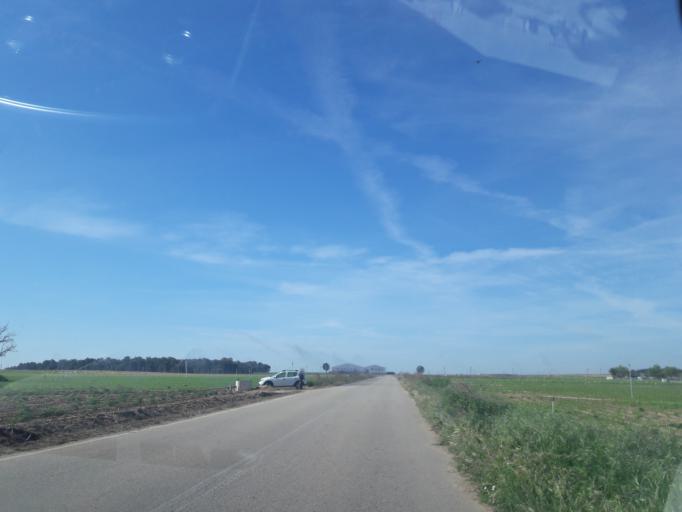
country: ES
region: Castille and Leon
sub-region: Provincia de Salamanca
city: Villoruela
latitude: 41.0406
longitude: -5.3868
